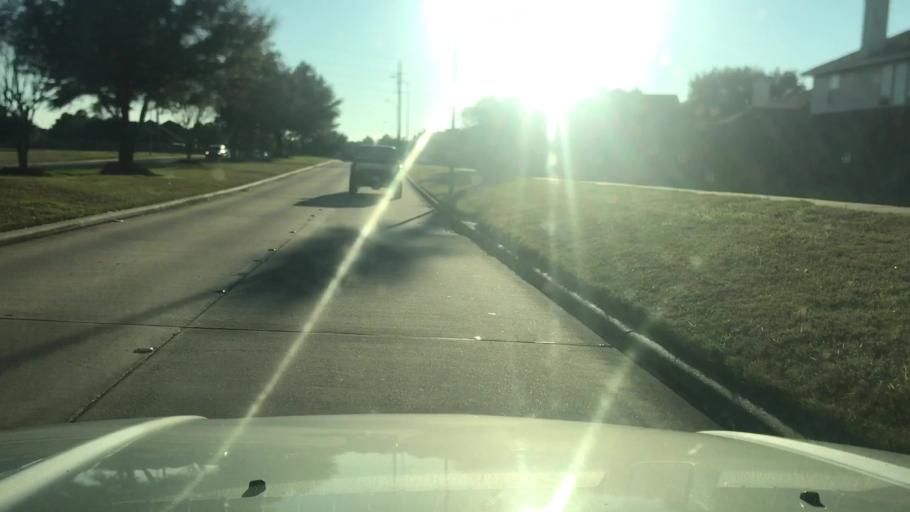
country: US
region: Texas
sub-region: Fort Bend County
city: Cinco Ranch
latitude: 29.7552
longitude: -95.7819
